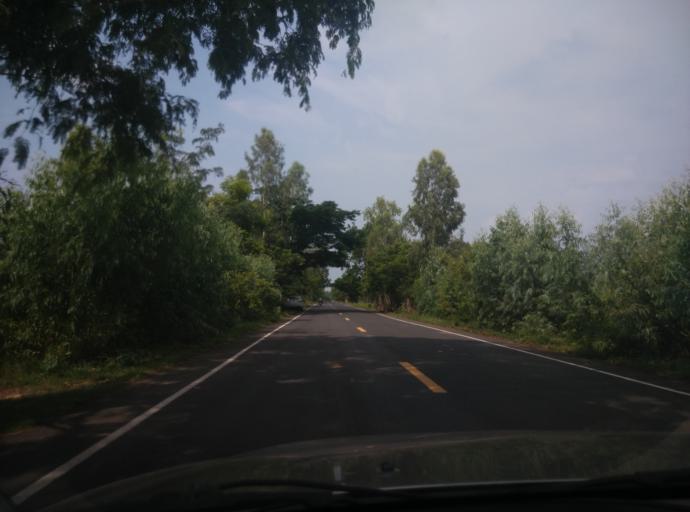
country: TH
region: Sisaket
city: Huai Thap Than
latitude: 15.0455
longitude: 104.0840
